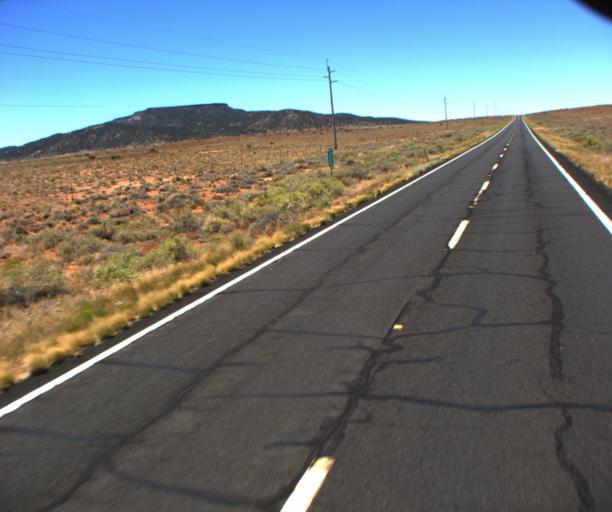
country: US
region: Arizona
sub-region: Coconino County
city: LeChee
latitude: 34.8877
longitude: -110.8738
